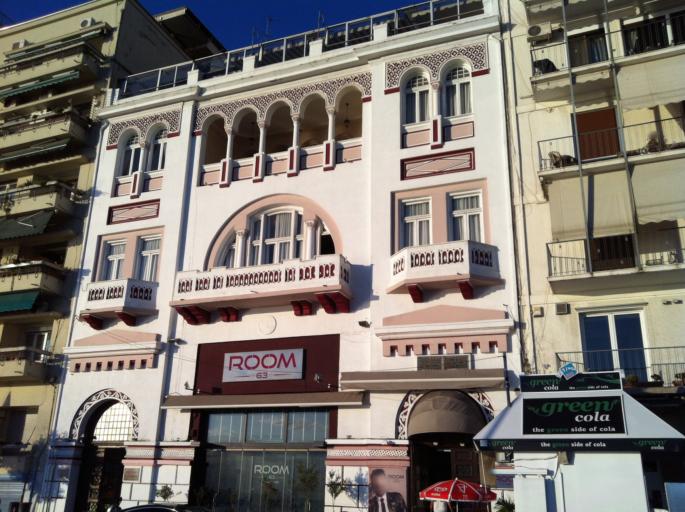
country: GR
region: Central Macedonia
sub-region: Nomos Thessalonikis
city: Agios Pavlos
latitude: 40.6283
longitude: 22.9458
